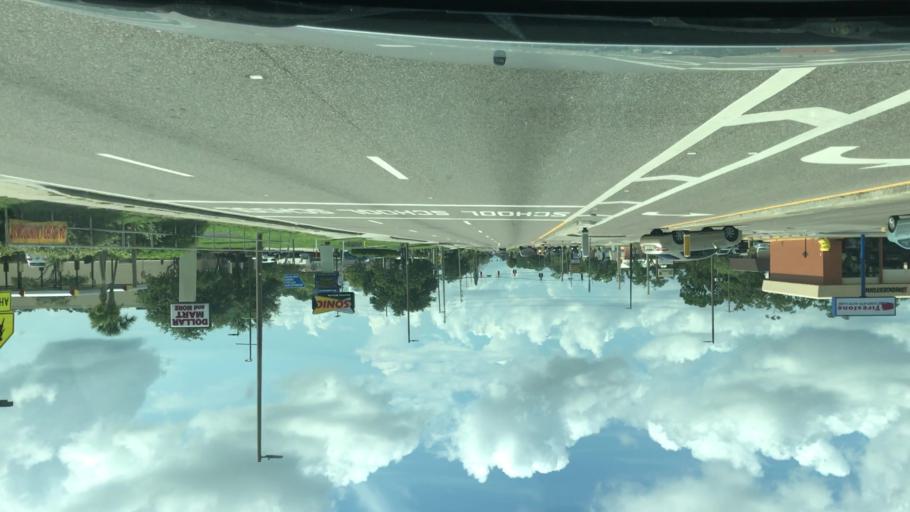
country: US
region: Florida
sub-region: Pinellas County
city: Pinellas Park
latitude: 27.8413
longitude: -82.6999
